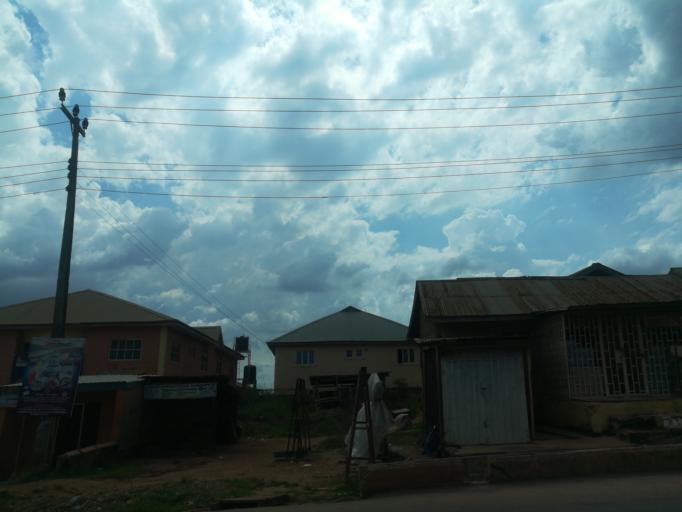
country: NG
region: Oyo
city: Ibadan
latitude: 7.4251
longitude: 3.8419
